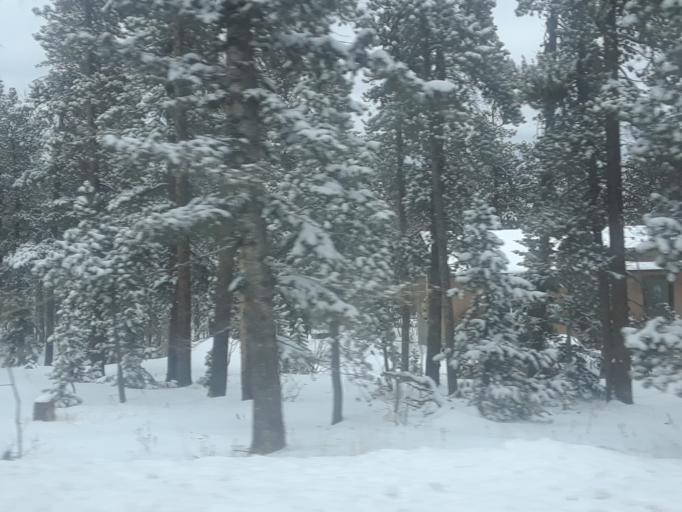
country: US
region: Colorado
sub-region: Boulder County
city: Coal Creek
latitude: 39.9253
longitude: -105.3907
